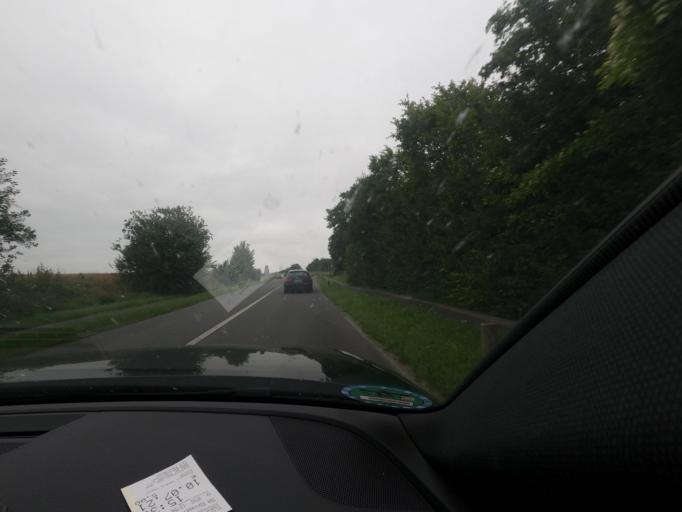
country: FR
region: Picardie
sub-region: Departement de la Somme
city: Cagny
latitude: 49.8627
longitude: 2.3091
